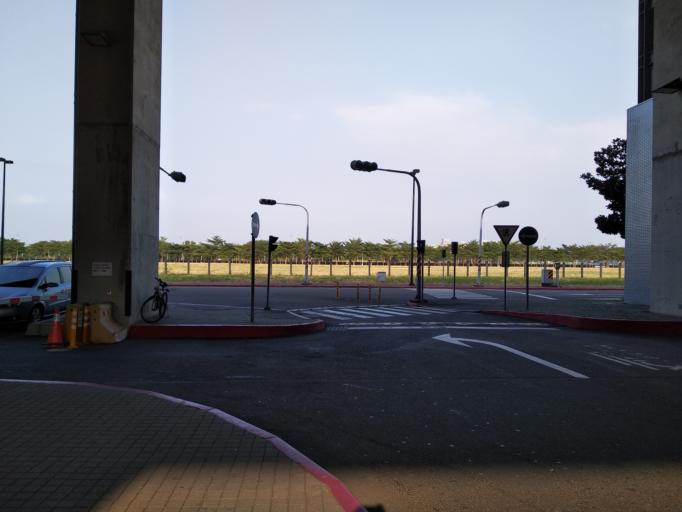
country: TW
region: Taiwan
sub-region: Tainan
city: Tainan
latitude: 22.9242
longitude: 120.2867
